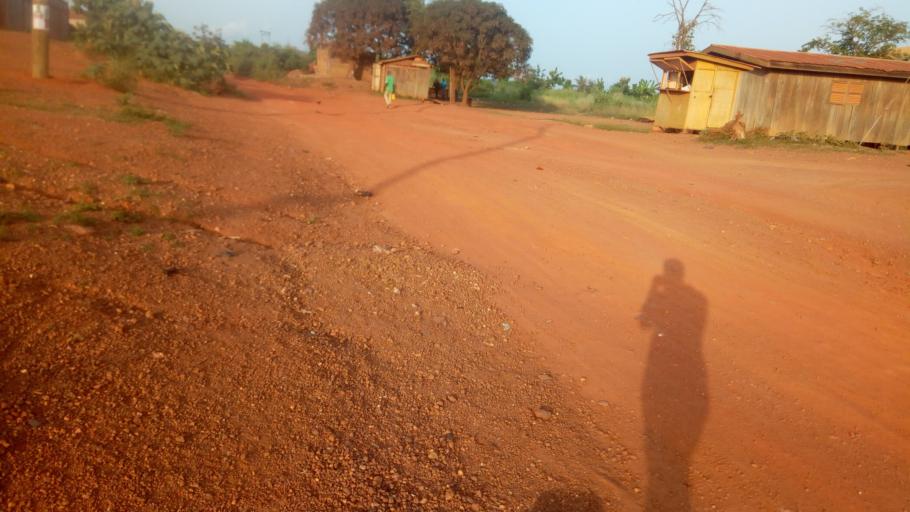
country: GH
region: Ashanti
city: Obuasi
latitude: 6.2122
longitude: -1.7007
